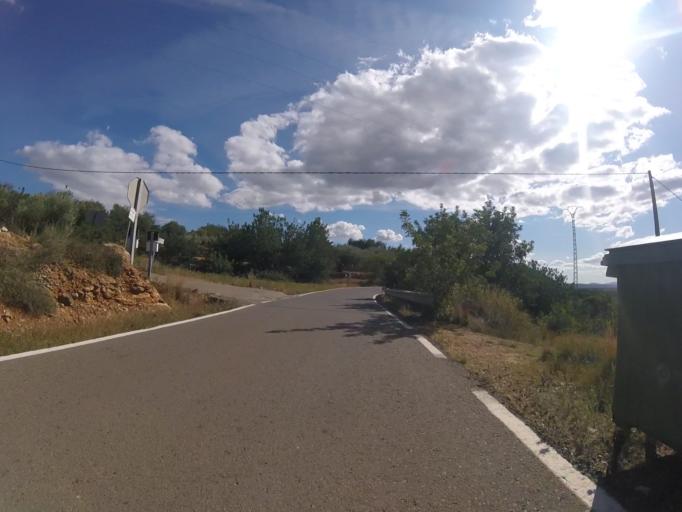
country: ES
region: Valencia
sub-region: Provincia de Castello
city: Cuevas de Vinroma
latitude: 40.3704
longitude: 0.1179
